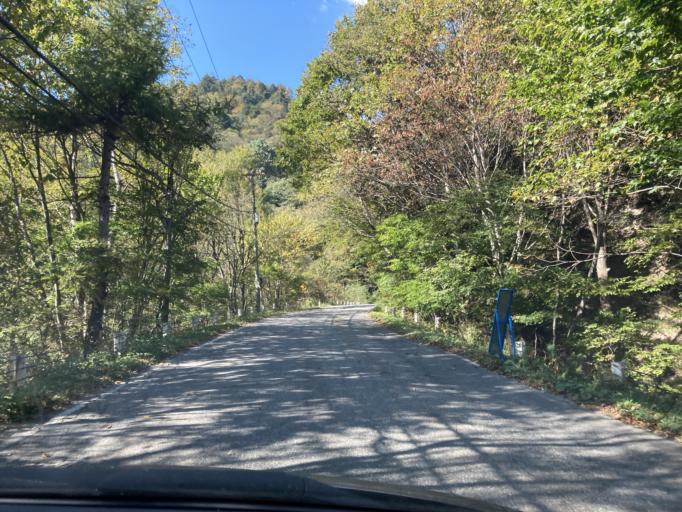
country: JP
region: Nagano
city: Omachi
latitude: 36.4905
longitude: 137.7415
